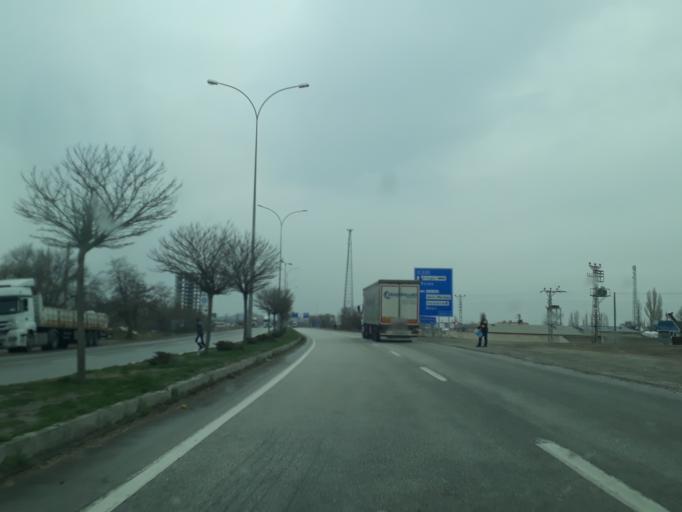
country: TR
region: Konya
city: Karapinar
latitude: 37.7155
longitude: 33.5766
